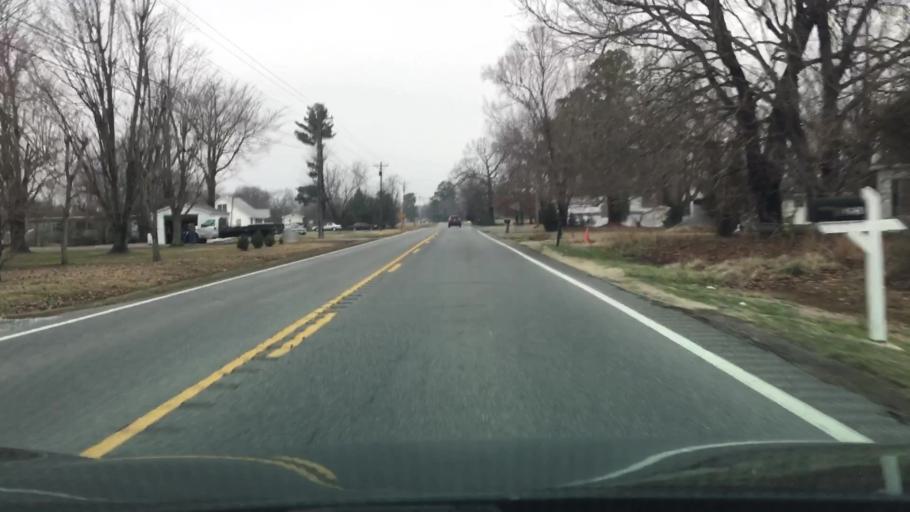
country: US
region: Kentucky
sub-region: Marshall County
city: Calvert City
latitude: 36.9697
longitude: -88.3884
